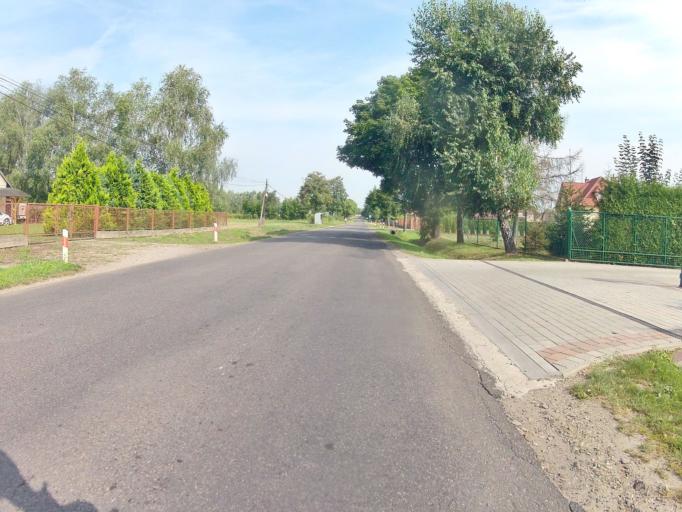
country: PL
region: Subcarpathian Voivodeship
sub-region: Powiat jasielski
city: Kolaczyce
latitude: 49.7816
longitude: 21.4046
